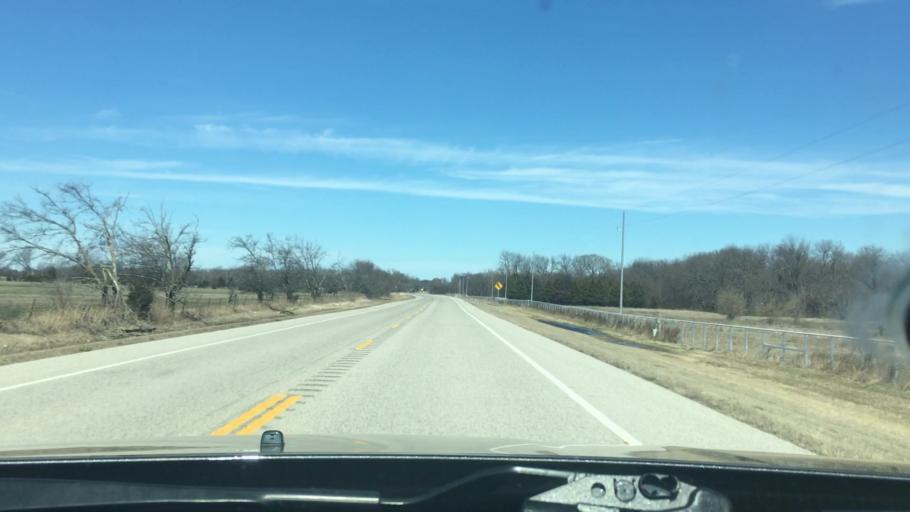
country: US
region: Oklahoma
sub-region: Murray County
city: Sulphur
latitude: 34.3834
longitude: -96.9508
